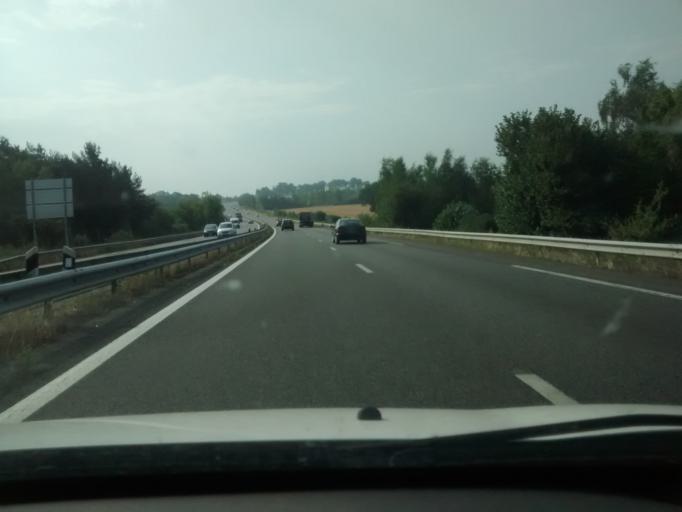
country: FR
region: Brittany
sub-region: Departement d'Ille-et-Vilaine
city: Bain-de-Bretagne
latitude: 47.8377
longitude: -1.6951
